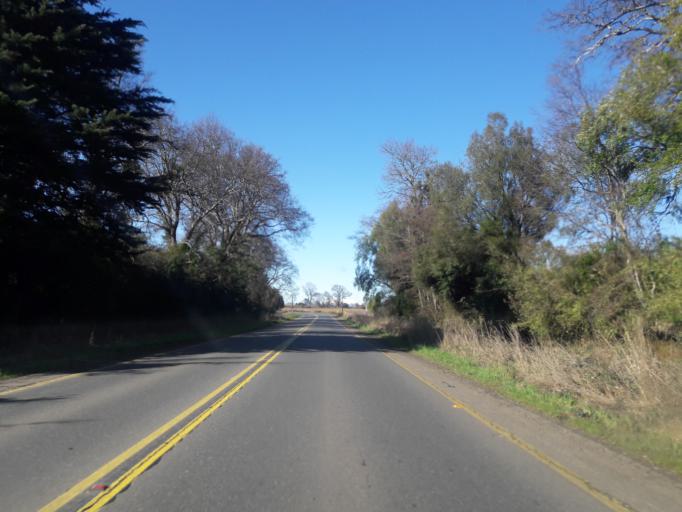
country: CL
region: Araucania
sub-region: Provincia de Malleco
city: Victoria
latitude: -38.2526
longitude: -72.2938
